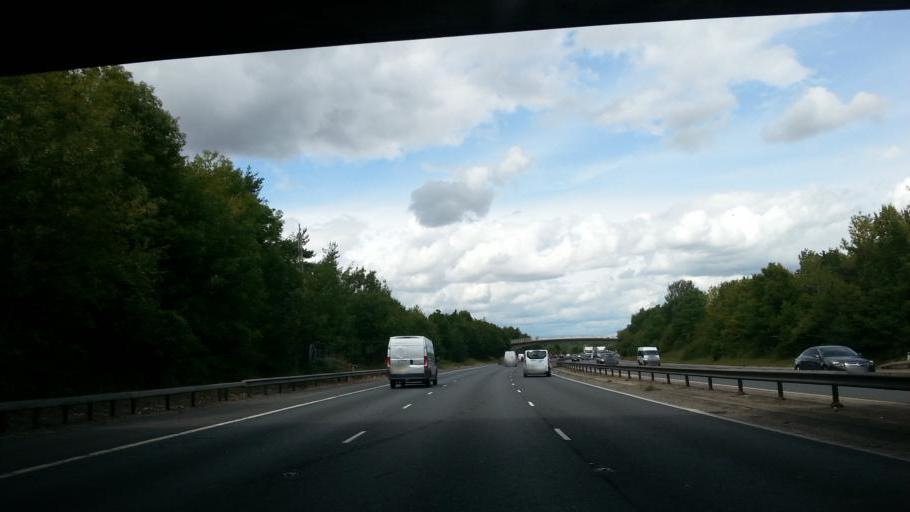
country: GB
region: England
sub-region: Essex
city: Little Hallingbury
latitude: 51.8500
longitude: 0.1848
